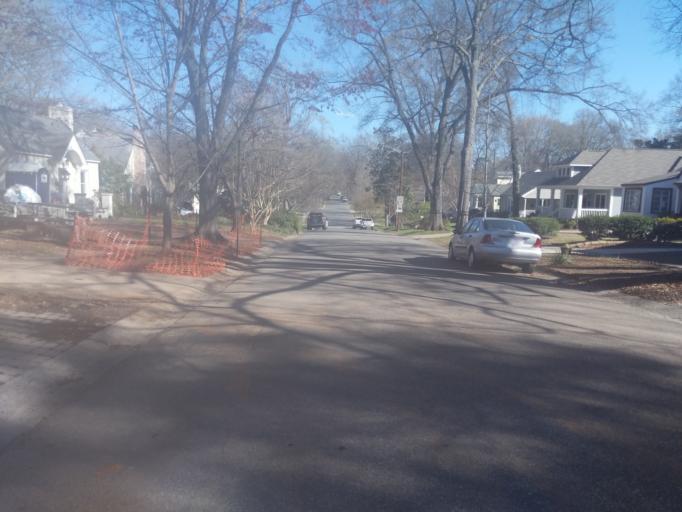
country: US
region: North Carolina
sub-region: Mecklenburg County
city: Charlotte
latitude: 35.2164
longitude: -80.8146
